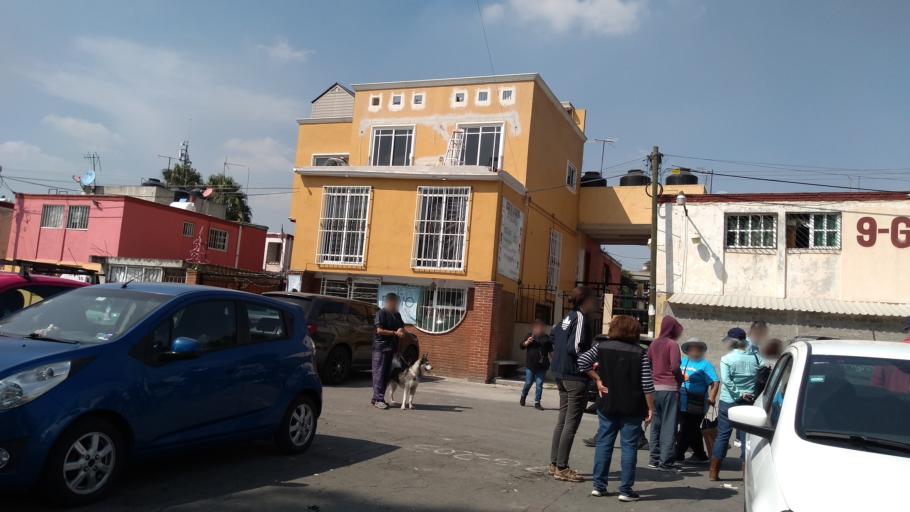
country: MX
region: Mexico City
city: Tlahuac
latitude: 19.2837
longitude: -99.0563
